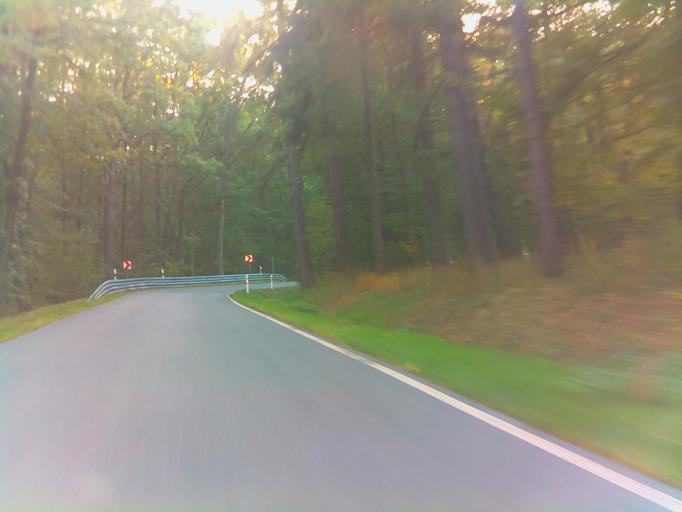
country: DE
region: Bavaria
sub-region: Regierungsbezirk Unterfranken
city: Hausen
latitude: 50.5108
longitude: 10.0957
